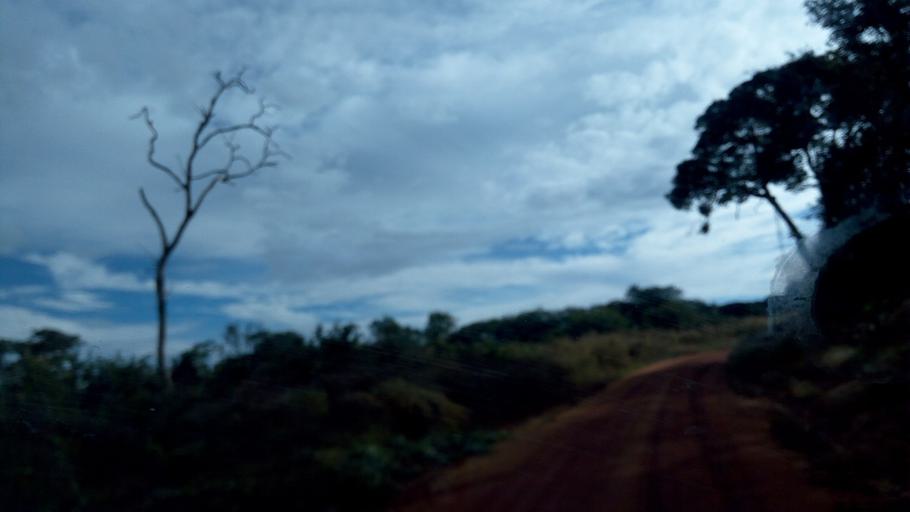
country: CD
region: Katanga
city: Kalemie
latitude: -6.4333
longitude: 29.0365
